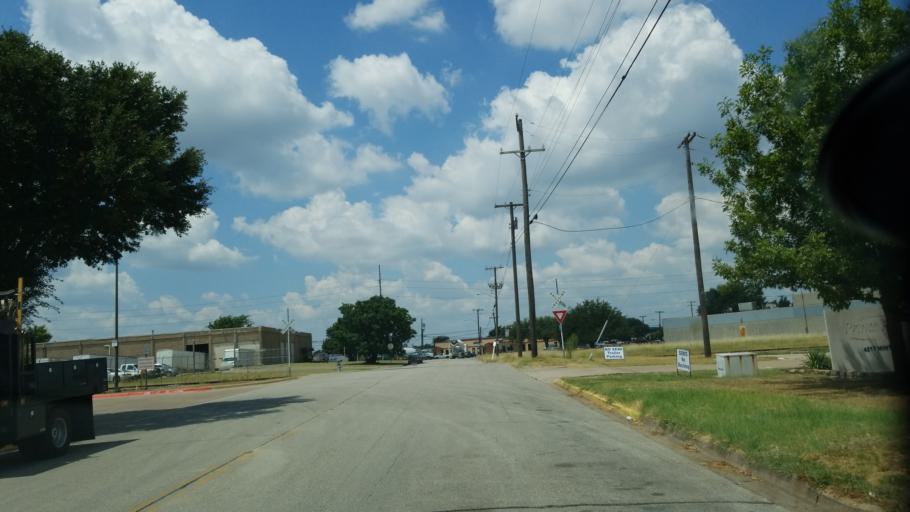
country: US
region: Texas
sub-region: Dallas County
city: Duncanville
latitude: 32.6851
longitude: -96.8895
